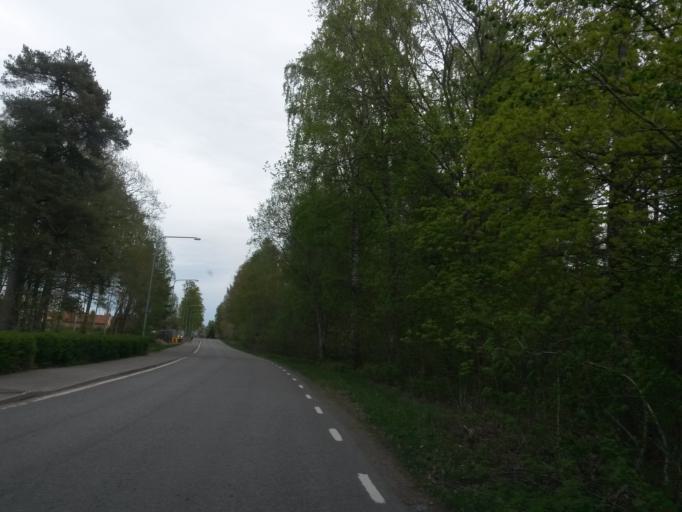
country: SE
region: Vaestra Goetaland
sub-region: Vara Kommun
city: Vara
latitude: 58.3277
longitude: 12.9088
